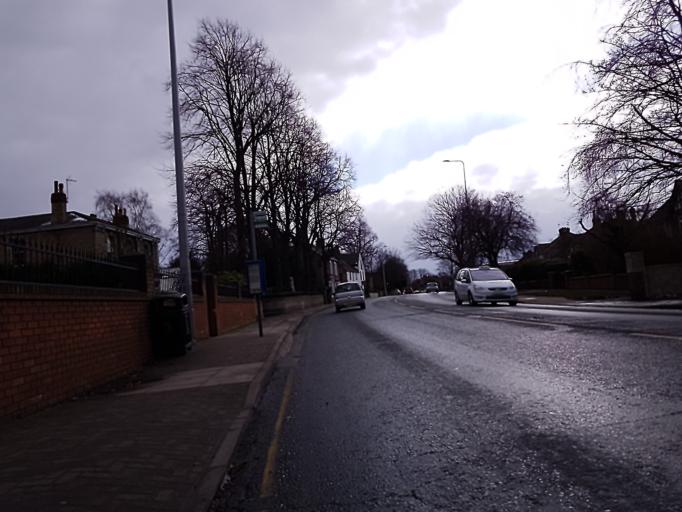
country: GB
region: England
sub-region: North East Lincolnshire
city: Grimbsy
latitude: 53.5588
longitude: -0.0919
